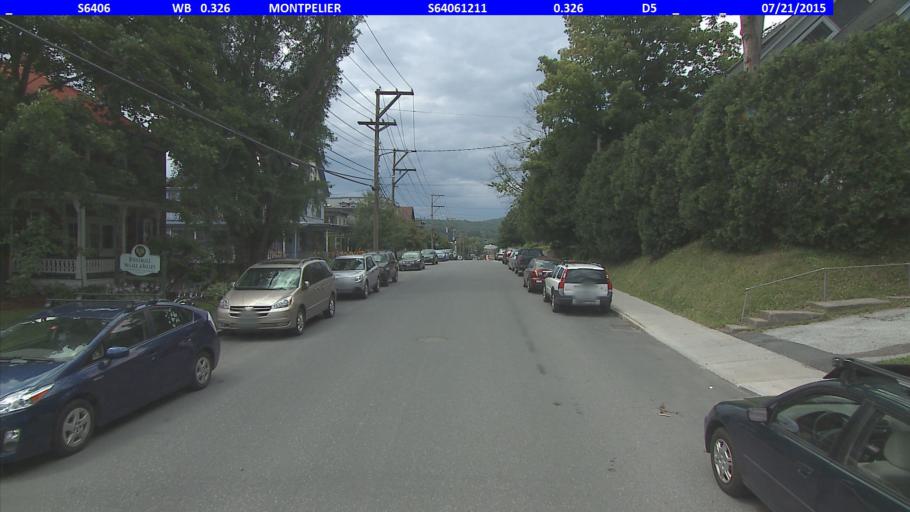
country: US
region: Vermont
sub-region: Washington County
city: Montpelier
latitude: 44.2553
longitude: -72.5722
